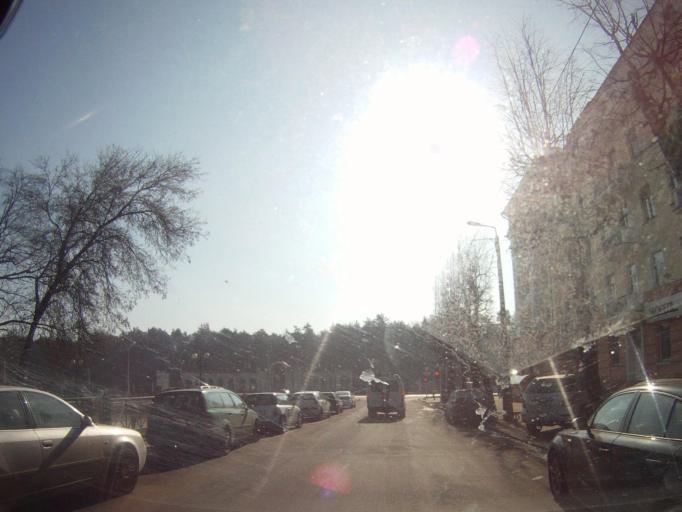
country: BY
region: Minsk
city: Minsk
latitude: 53.9249
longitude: 27.6141
